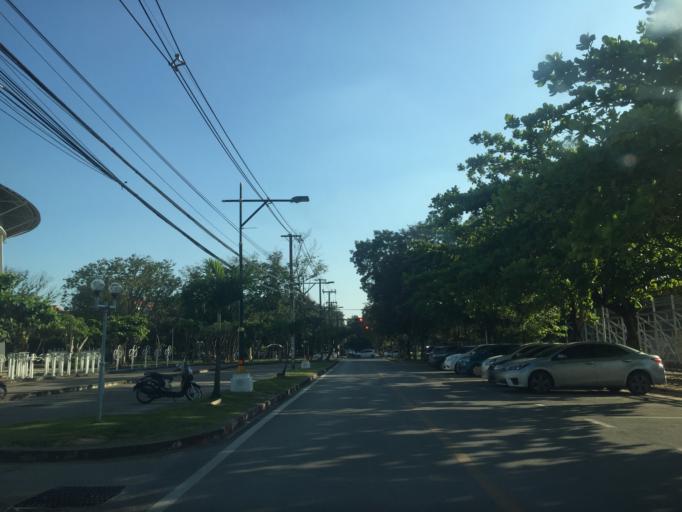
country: TH
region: Chiang Mai
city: Chiang Mai
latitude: 18.7970
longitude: 98.9573
